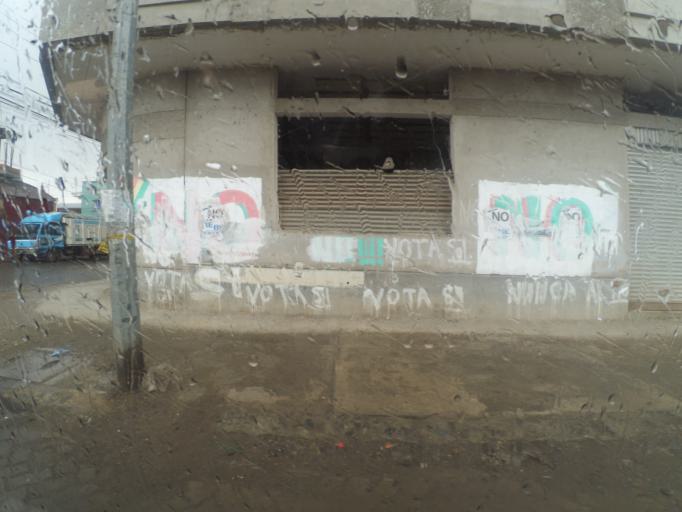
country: BO
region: La Paz
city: La Paz
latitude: -16.5200
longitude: -68.1667
